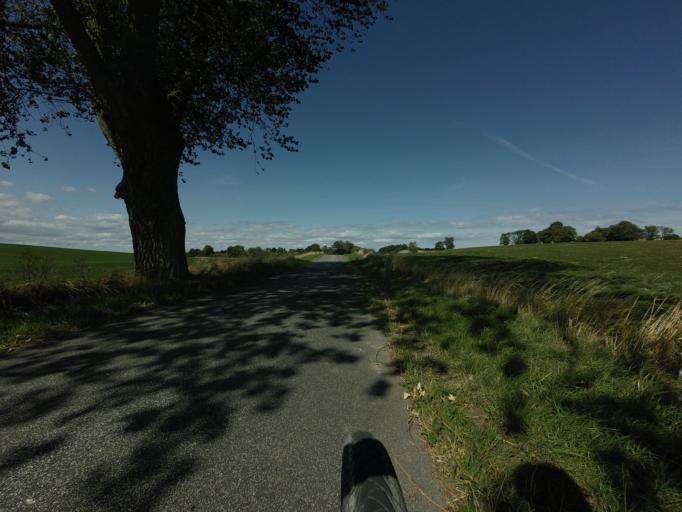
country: DK
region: Zealand
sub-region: Vordingborg Kommune
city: Stege
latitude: 54.9995
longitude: 12.4771
